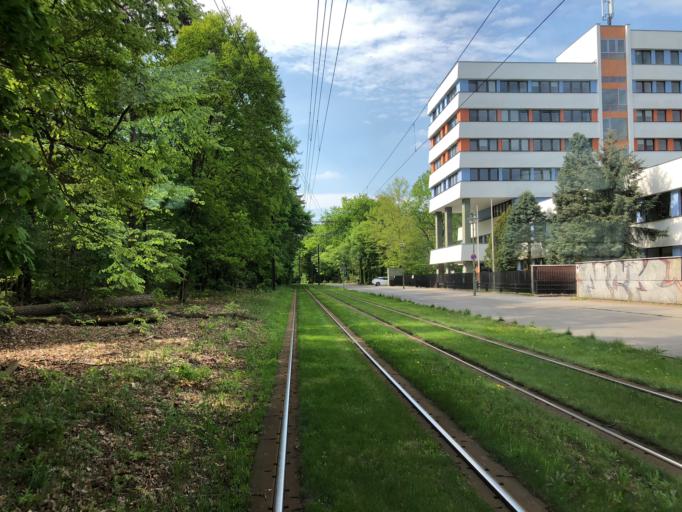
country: DE
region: Berlin
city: Grunau
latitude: 52.4094
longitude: 13.6025
